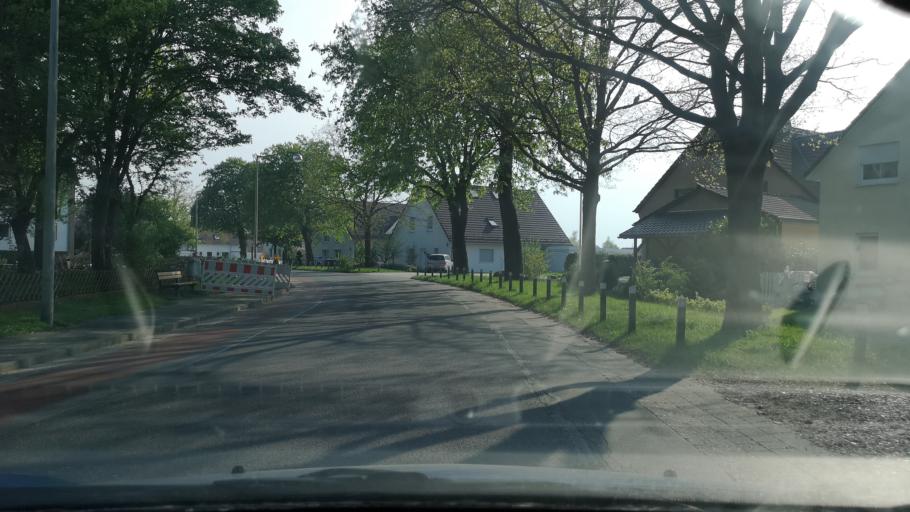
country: DE
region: Lower Saxony
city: Langenhagen
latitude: 52.4457
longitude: 9.6754
